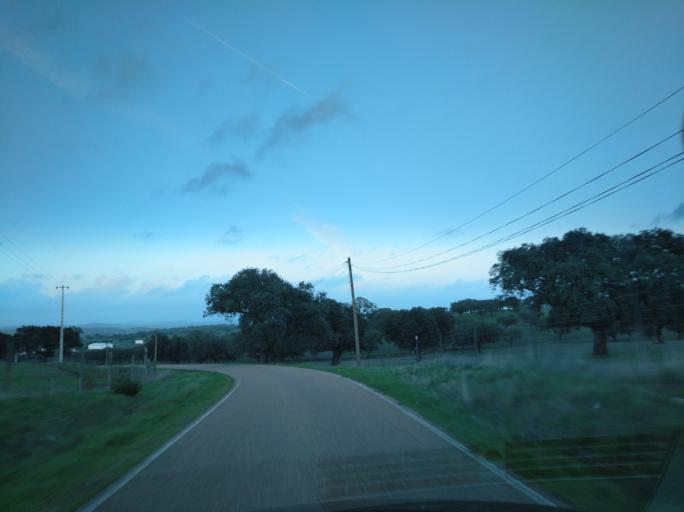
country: PT
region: Portalegre
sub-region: Campo Maior
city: Campo Maior
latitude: 39.0707
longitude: -7.1158
